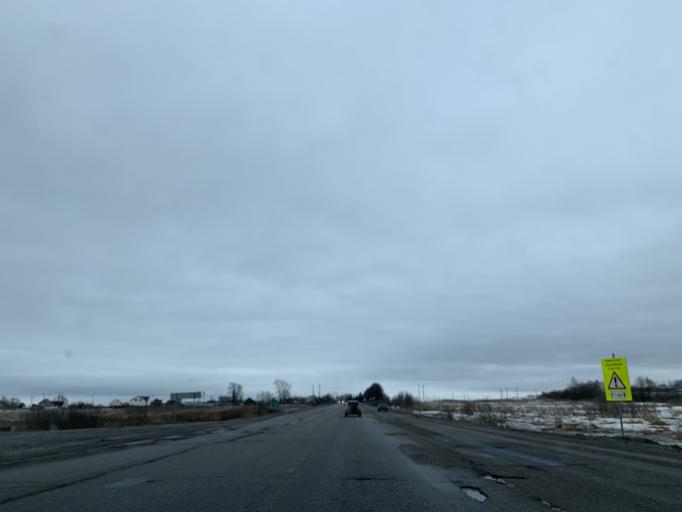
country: RU
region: Jaroslavl
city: Konstantinovskiy
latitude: 57.7935
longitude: 39.6039
